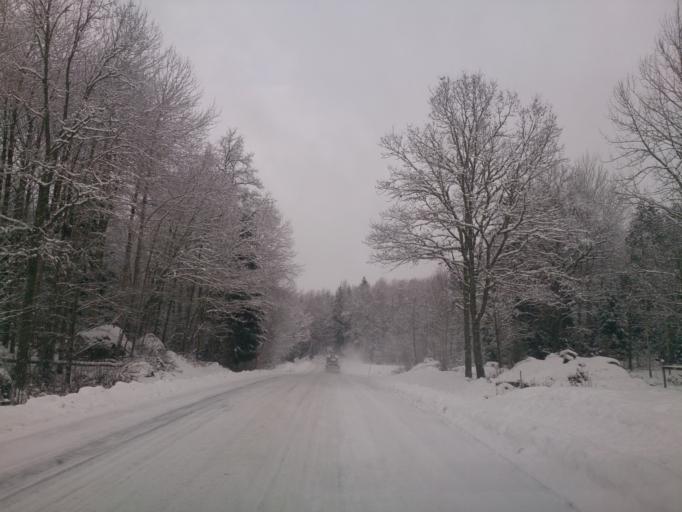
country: SE
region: OEstergoetland
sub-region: Atvidabergs Kommun
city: Atvidaberg
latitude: 58.2799
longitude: 16.0351
